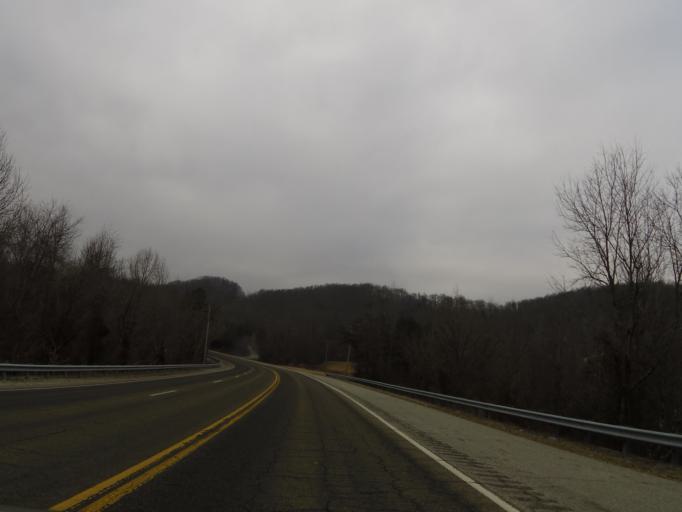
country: US
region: Tennessee
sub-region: Morgan County
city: Wartburg
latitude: 36.1158
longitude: -84.6020
